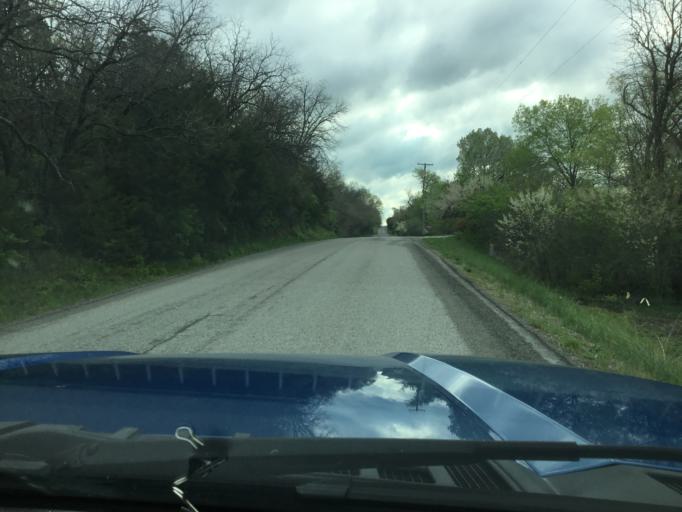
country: US
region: Kansas
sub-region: Douglas County
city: Lawrence
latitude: 38.9282
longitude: -95.1994
